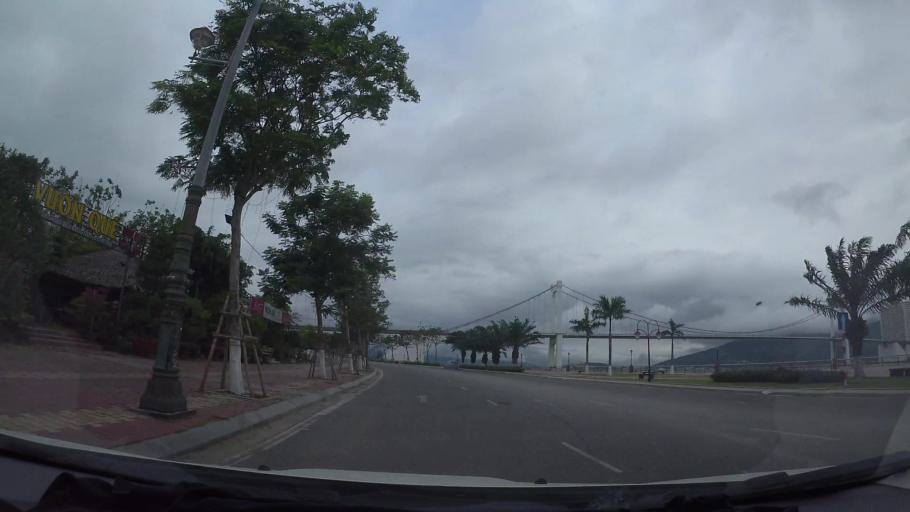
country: VN
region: Da Nang
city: Da Nang
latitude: 16.0908
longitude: 108.2194
